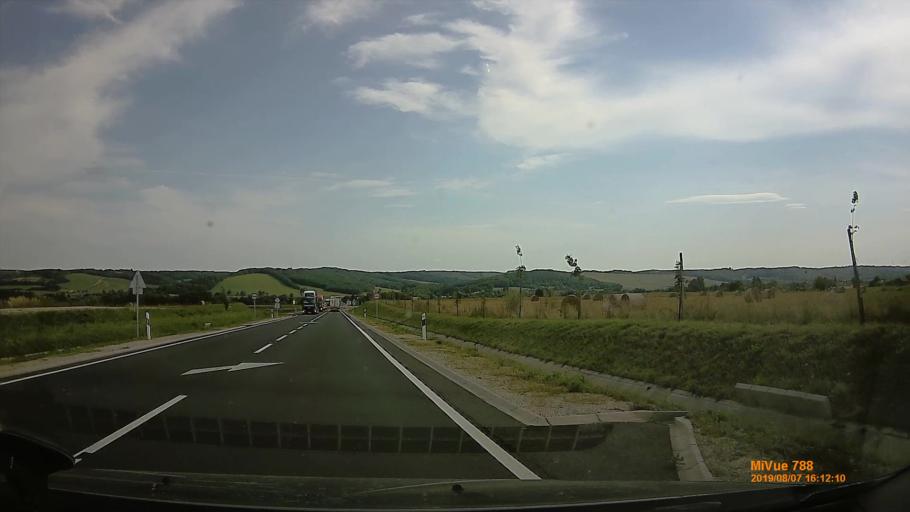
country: HU
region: Zala
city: Zalalovo
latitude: 46.8597
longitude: 16.6270
